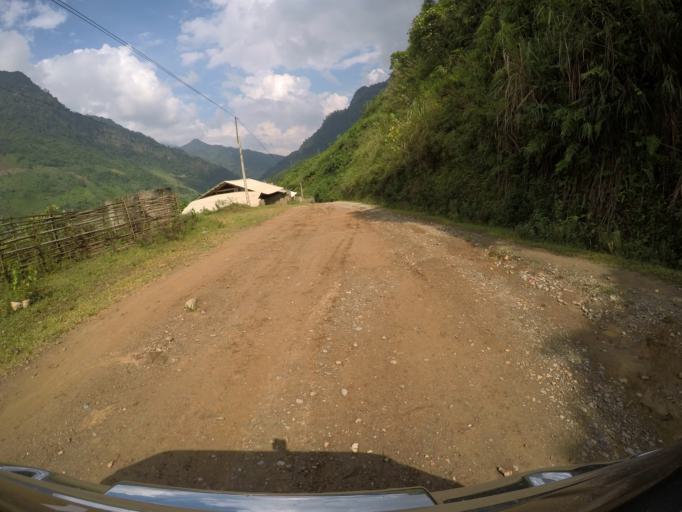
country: VN
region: Yen Bai
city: Son Thinh
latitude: 21.6787
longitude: 104.5509
